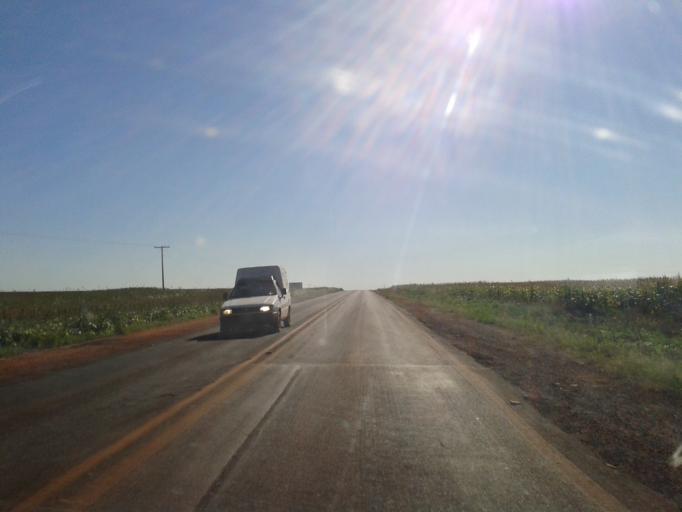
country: BR
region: Minas Gerais
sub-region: Capinopolis
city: Capinopolis
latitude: -18.6586
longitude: -49.5554
